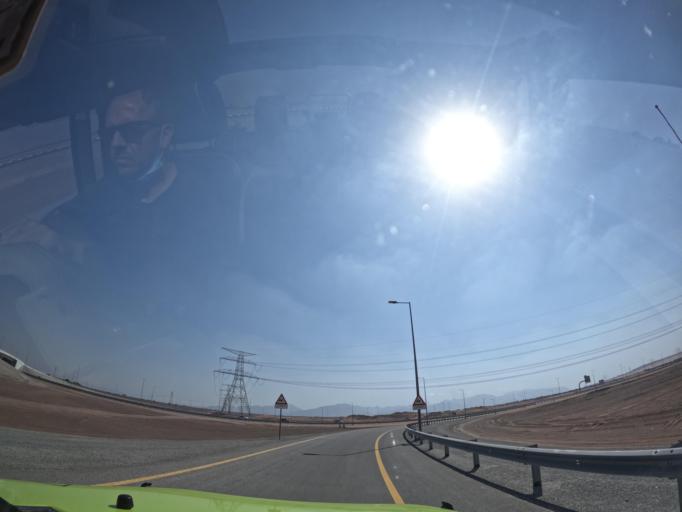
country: AE
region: Ash Shariqah
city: Adh Dhayd
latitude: 24.8125
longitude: 55.8005
